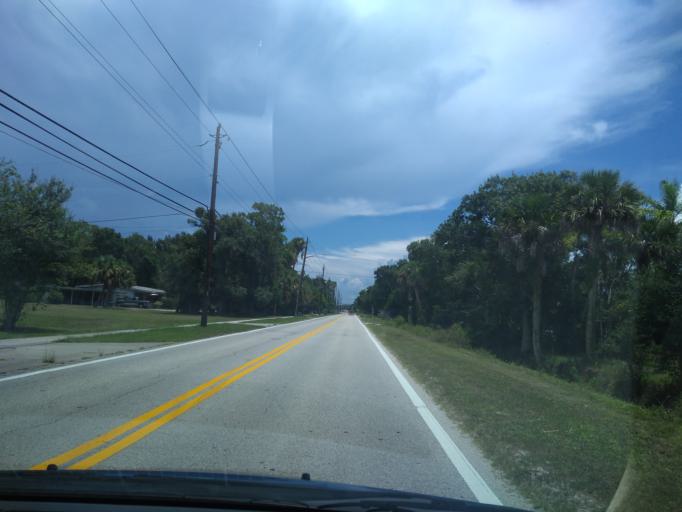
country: US
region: Florida
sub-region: Indian River County
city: Vero Beach South
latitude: 27.6309
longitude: -80.4101
